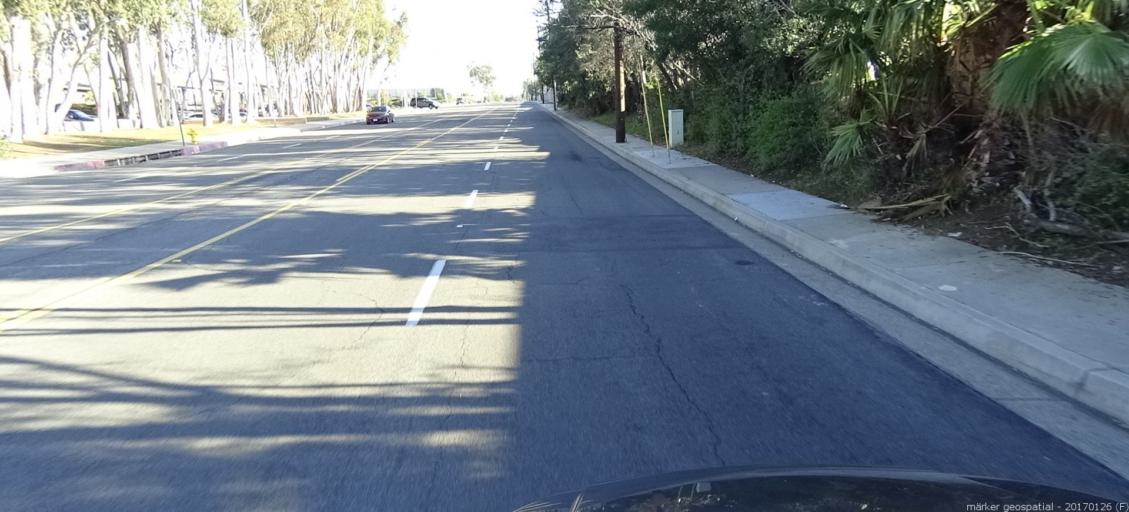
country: US
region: California
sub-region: Orange County
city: Lake Forest
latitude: 33.6369
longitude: -117.6908
